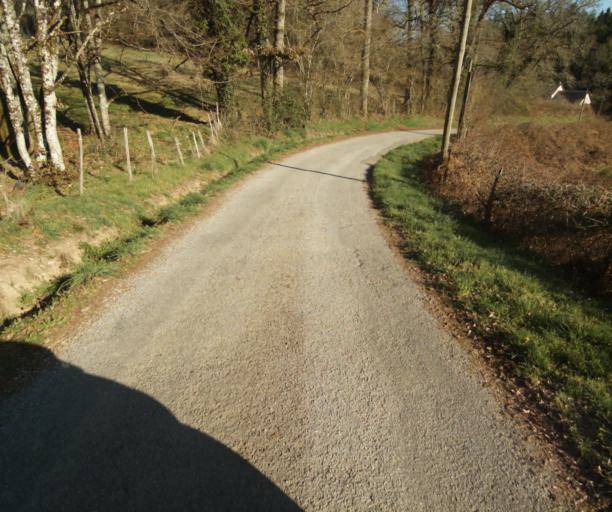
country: FR
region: Limousin
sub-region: Departement de la Correze
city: Chamboulive
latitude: 45.4932
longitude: 1.7265
